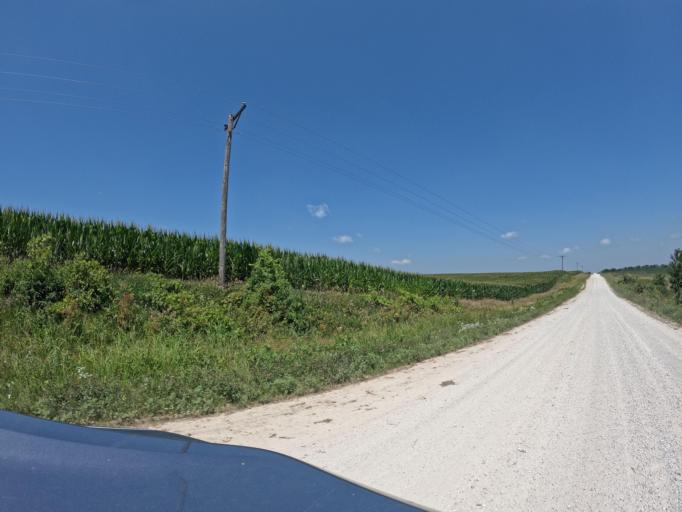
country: US
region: Iowa
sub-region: Keokuk County
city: Sigourney
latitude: 41.2749
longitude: -92.2381
